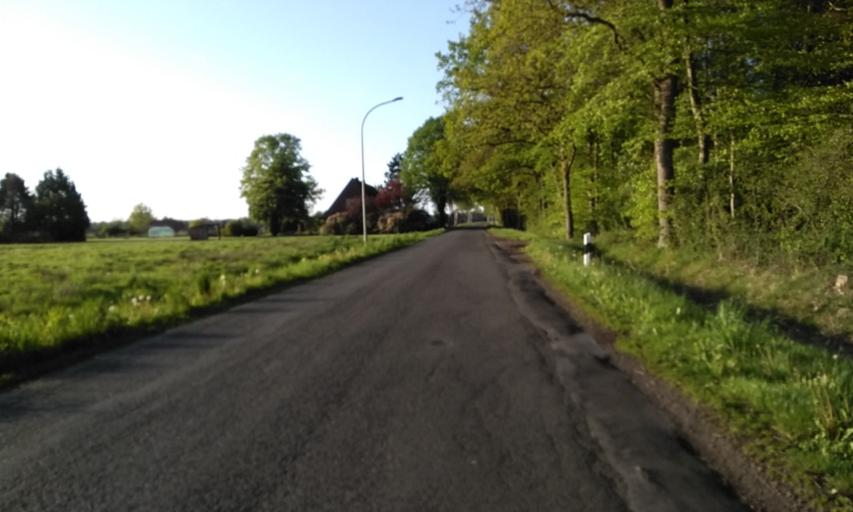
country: DE
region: Lower Saxony
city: Ahlerstedt
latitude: 53.3991
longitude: 9.5047
